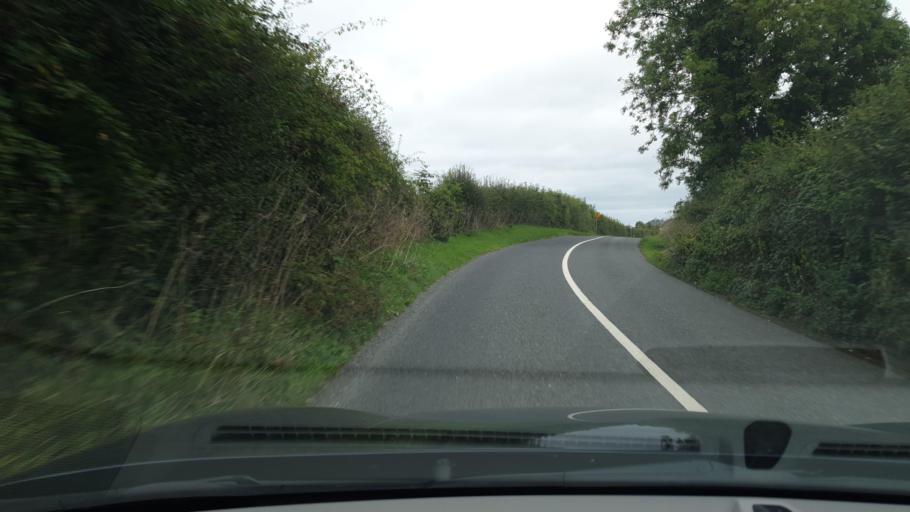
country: IE
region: Leinster
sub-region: Kildare
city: Kilcock
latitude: 53.4315
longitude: -6.6506
